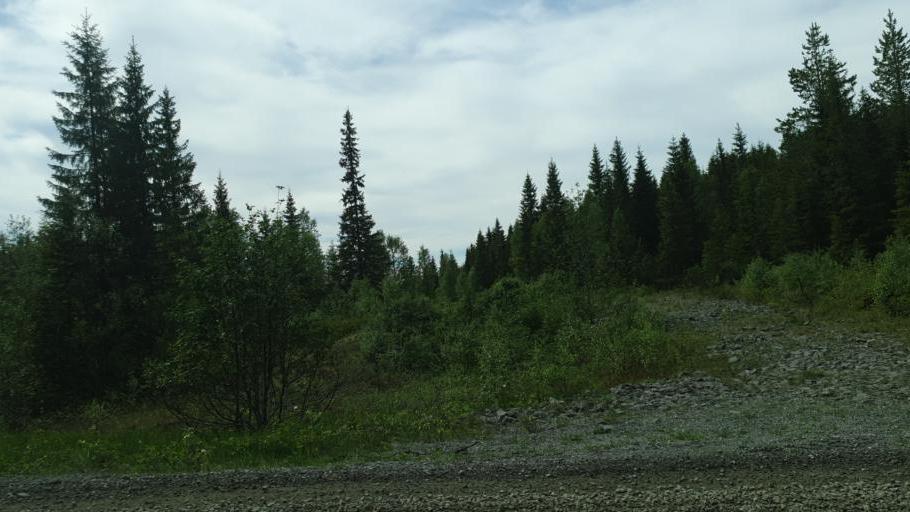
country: NO
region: Nord-Trondelag
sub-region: Leksvik
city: Leksvik
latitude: 63.6917
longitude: 10.4508
